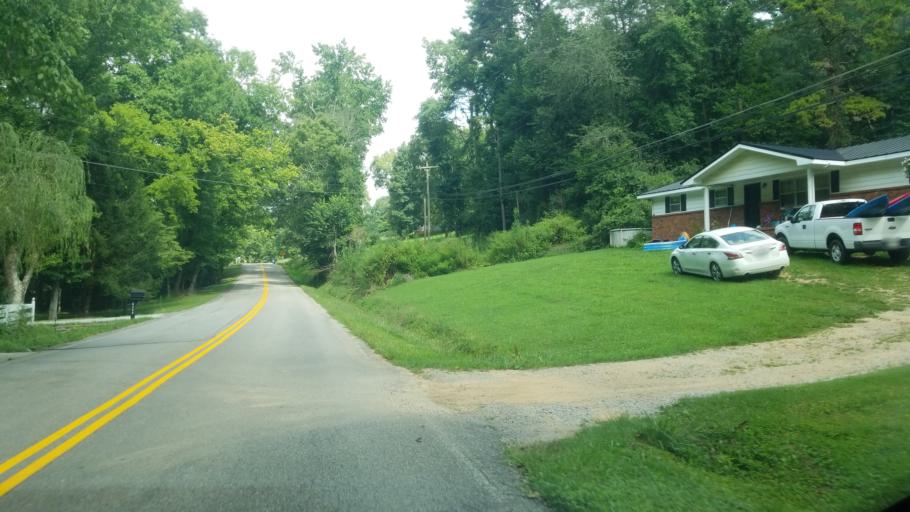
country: US
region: Tennessee
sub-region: Hamilton County
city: Lakesite
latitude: 35.1849
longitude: -85.1006
